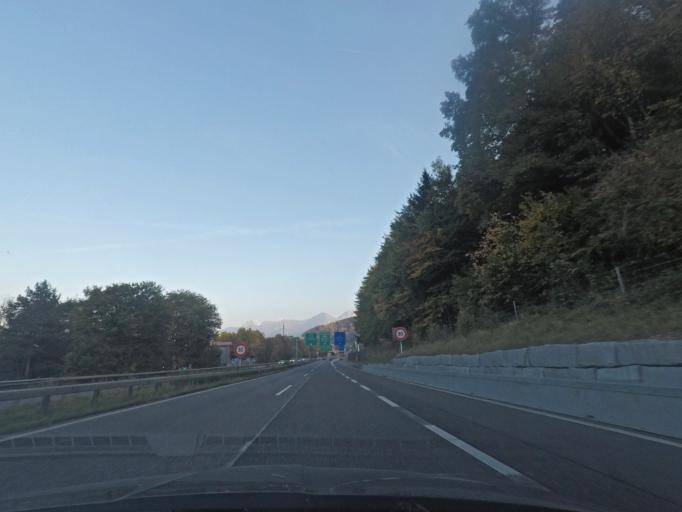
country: CH
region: Bern
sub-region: Frutigen-Niedersimmental District
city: Spiez
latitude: 46.6874
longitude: 7.6651
